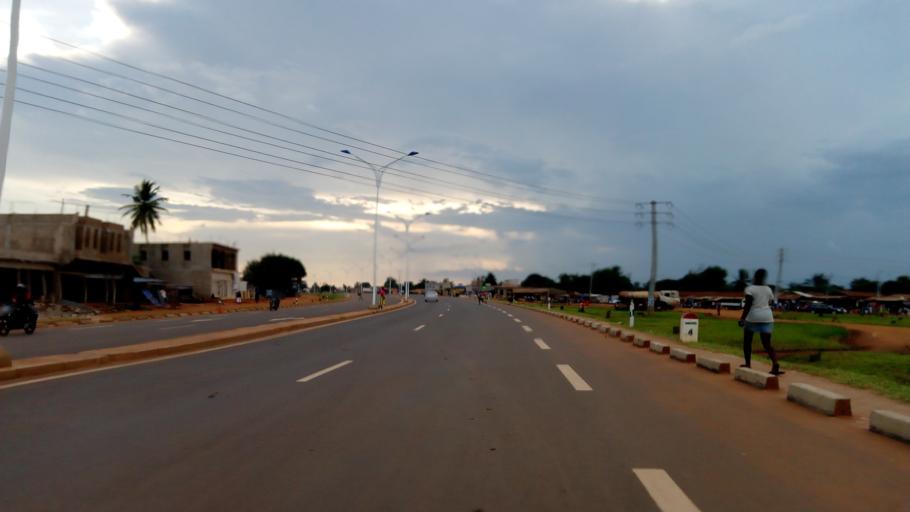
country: TG
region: Maritime
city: Lome
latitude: 6.2674
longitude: 1.1518
